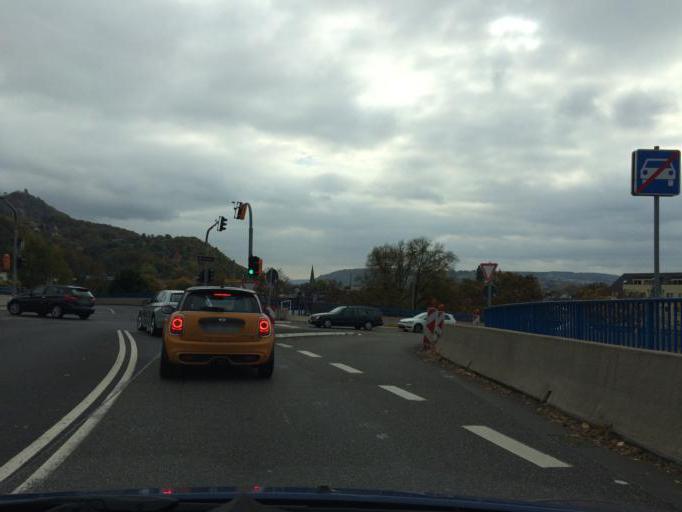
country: DE
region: North Rhine-Westphalia
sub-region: Regierungsbezirk Koln
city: Konigswinter
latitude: 50.6790
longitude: 7.1945
